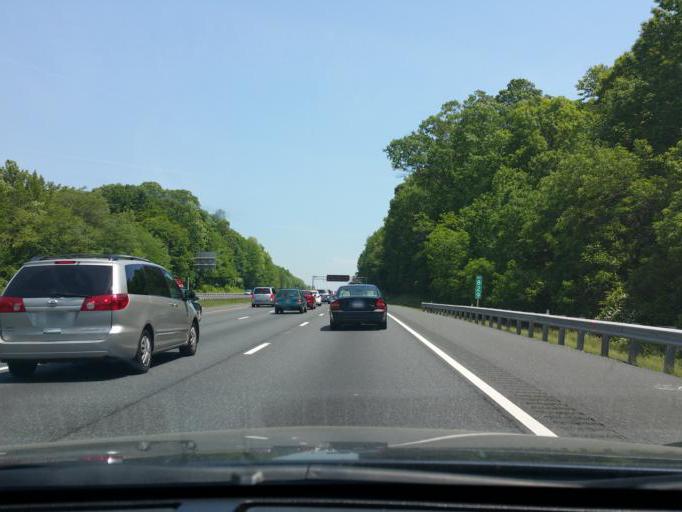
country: US
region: Maryland
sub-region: Harford County
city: Perryman
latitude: 39.5074
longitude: -76.2126
